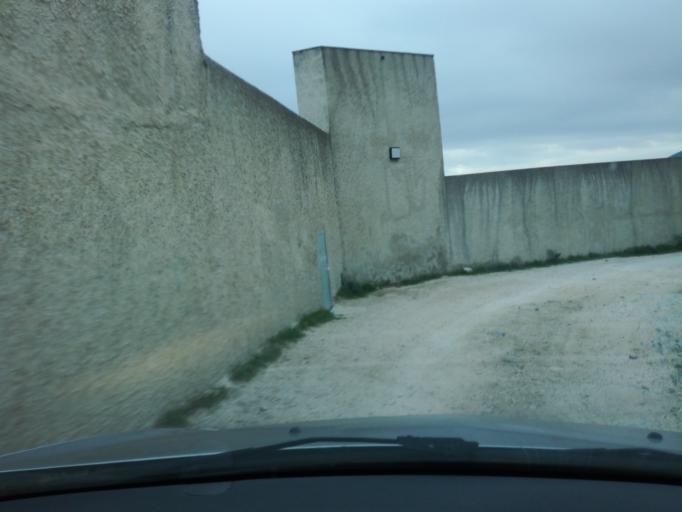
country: FR
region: Provence-Alpes-Cote d'Azur
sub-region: Departement du Var
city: Hyeres
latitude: 43.1242
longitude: 6.1265
